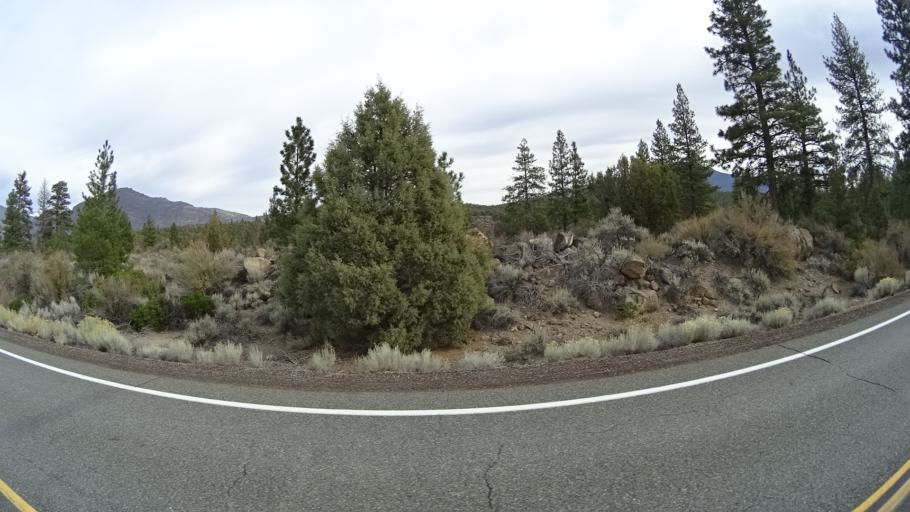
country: US
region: California
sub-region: Siskiyou County
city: Weed
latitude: 41.5487
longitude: -122.2484
